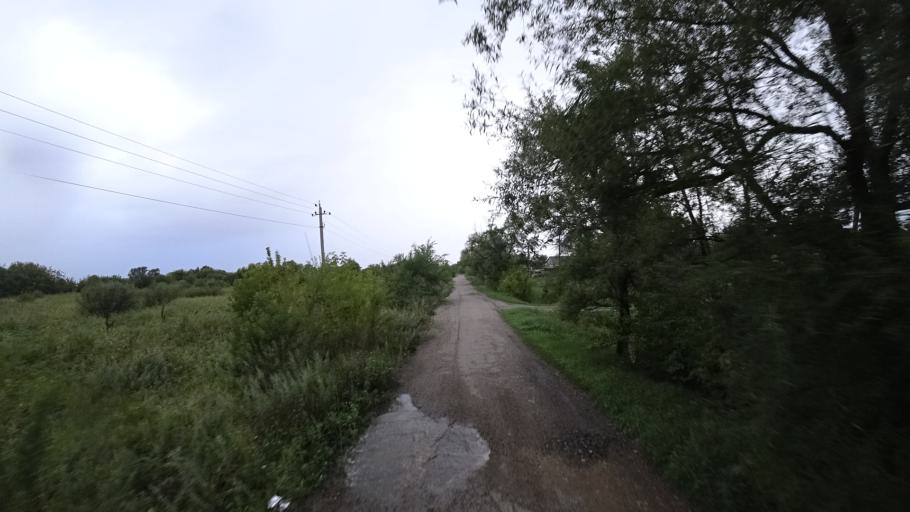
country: RU
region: Primorskiy
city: Chernigovka
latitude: 44.4008
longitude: 132.5314
